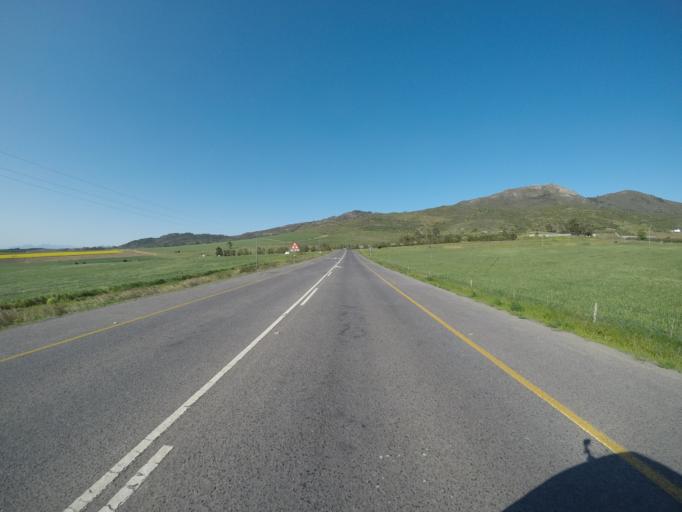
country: ZA
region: Western Cape
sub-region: Cape Winelands District Municipality
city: Noorder-Paarl
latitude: -33.7079
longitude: 18.8904
